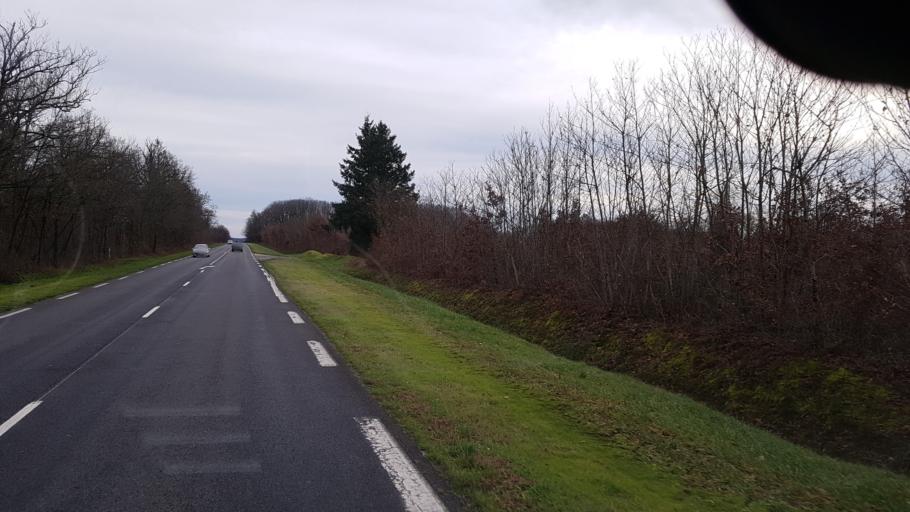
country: FR
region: Centre
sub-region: Departement du Loir-et-Cher
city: Lamotte-Beuvron
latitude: 47.6220
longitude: 2.0119
